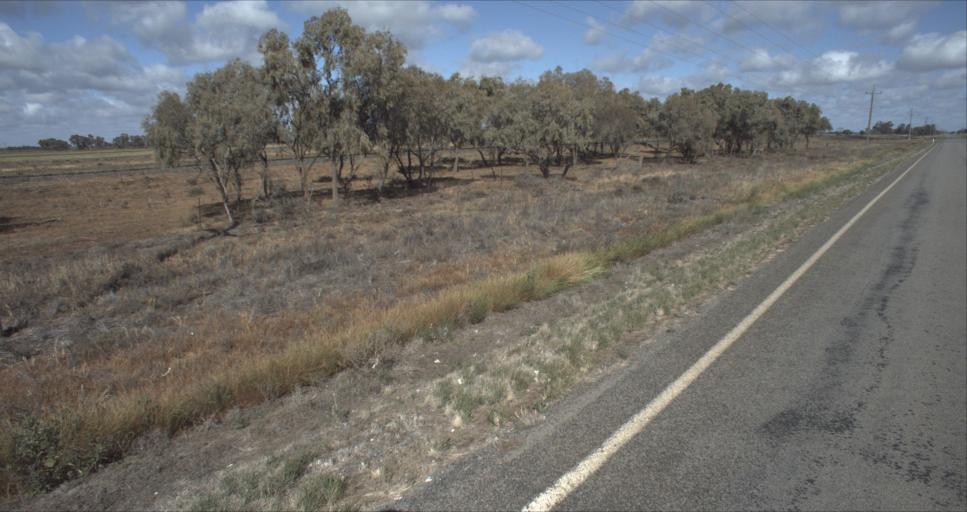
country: AU
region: New South Wales
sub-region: Leeton
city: Leeton
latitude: -34.5403
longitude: 146.2444
